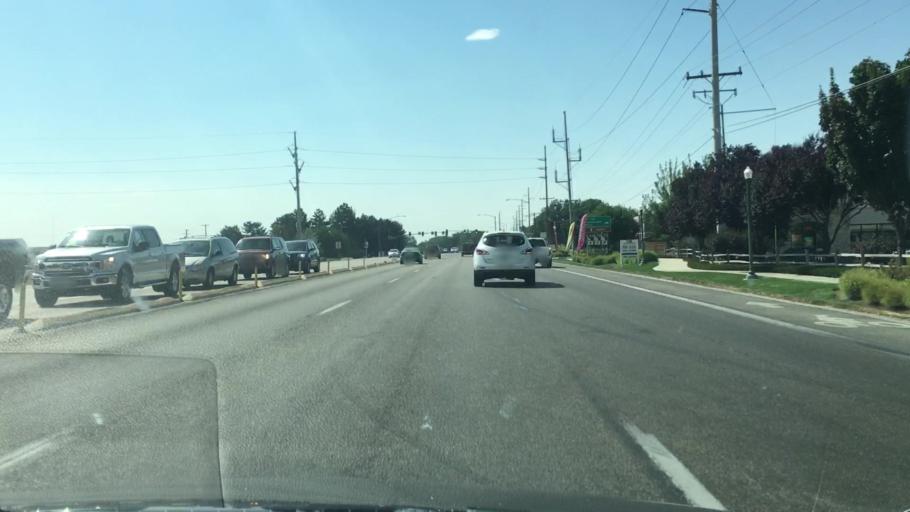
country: US
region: Idaho
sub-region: Ada County
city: Eagle
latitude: 43.6837
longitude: -116.3171
